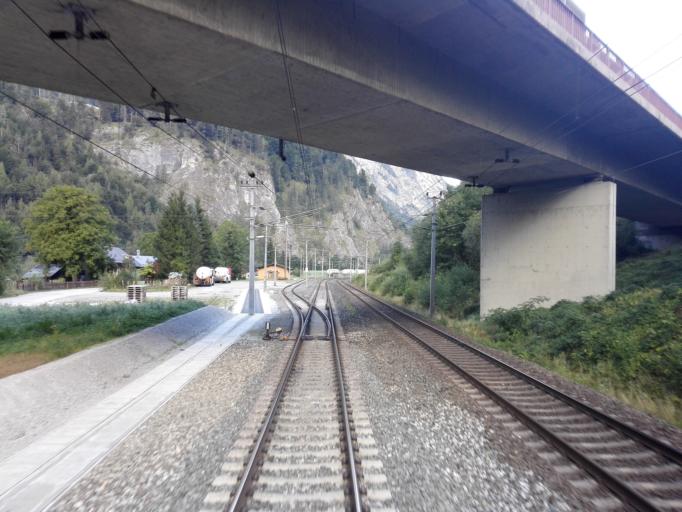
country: AT
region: Salzburg
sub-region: Politischer Bezirk Sankt Johann im Pongau
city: Werfen
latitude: 47.5224
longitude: 13.1672
